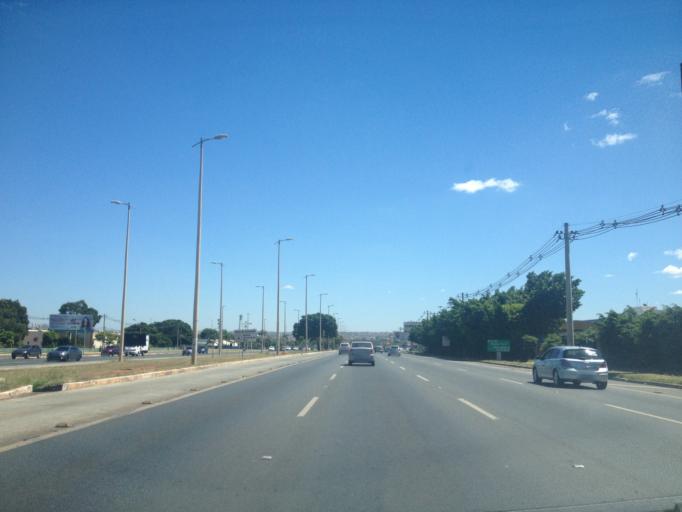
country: BR
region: Federal District
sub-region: Brasilia
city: Brasilia
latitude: -15.8084
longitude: -47.9589
